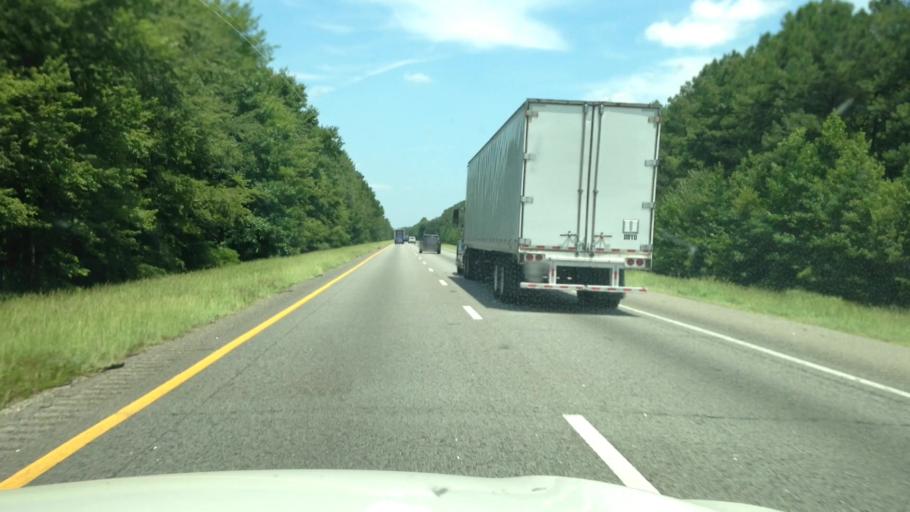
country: US
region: South Carolina
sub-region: Dillon County
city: Latta
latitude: 34.3158
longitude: -79.5982
